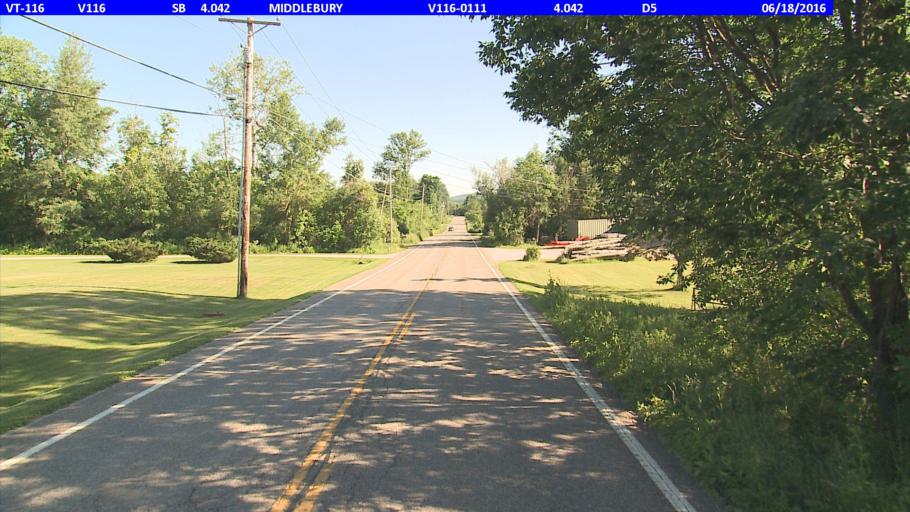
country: US
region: Vermont
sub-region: Addison County
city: Middlebury (village)
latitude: 44.0207
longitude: -73.1026
